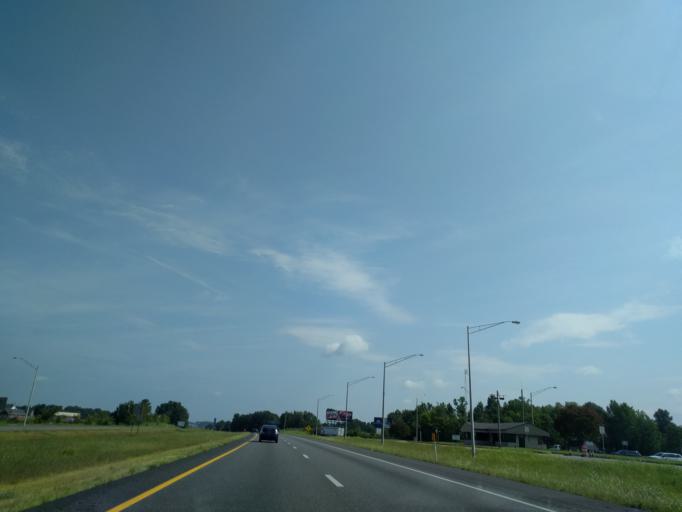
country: US
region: Tennessee
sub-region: Sumner County
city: Portland
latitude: 36.6087
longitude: -86.5810
